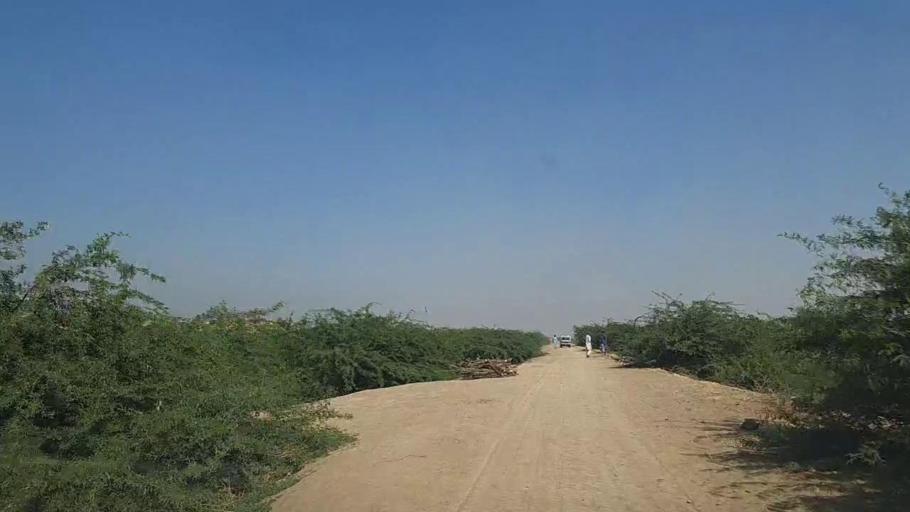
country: PK
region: Sindh
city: Daro Mehar
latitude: 24.8717
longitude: 68.0482
